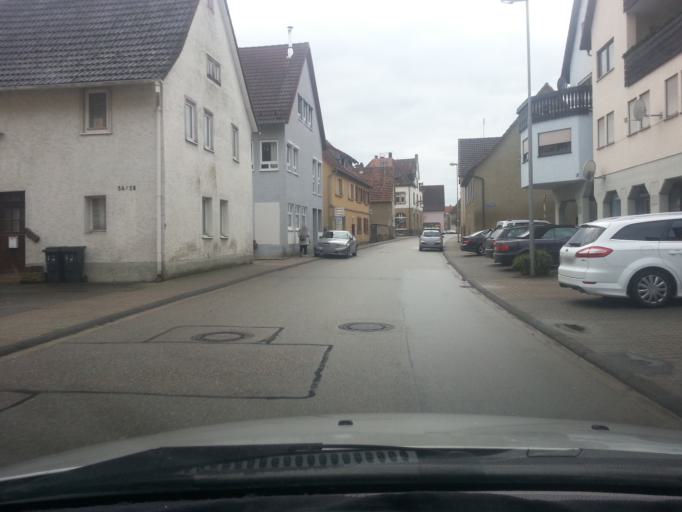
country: DE
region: Baden-Wuerttemberg
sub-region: Regierungsbezirk Stuttgart
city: Ittlingen
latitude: 49.1907
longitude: 8.9333
